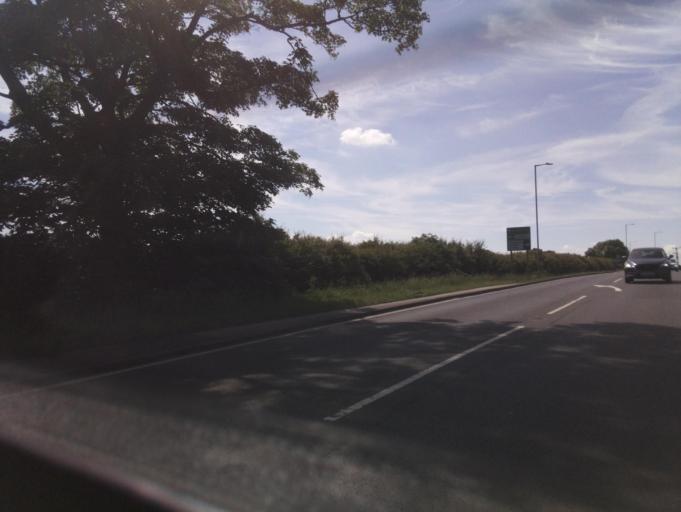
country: GB
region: England
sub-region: Lincolnshire
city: Burton
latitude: 53.2932
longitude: -0.5409
